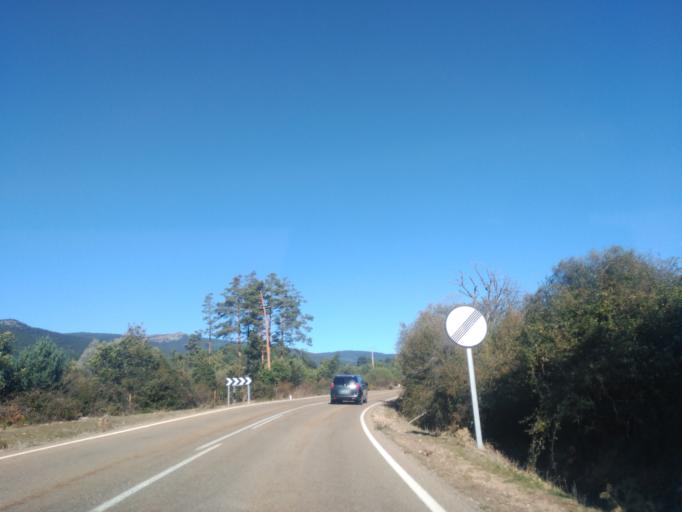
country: ES
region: Castille and Leon
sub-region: Provincia de Soria
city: Vinuesa
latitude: 41.9627
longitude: -2.7794
